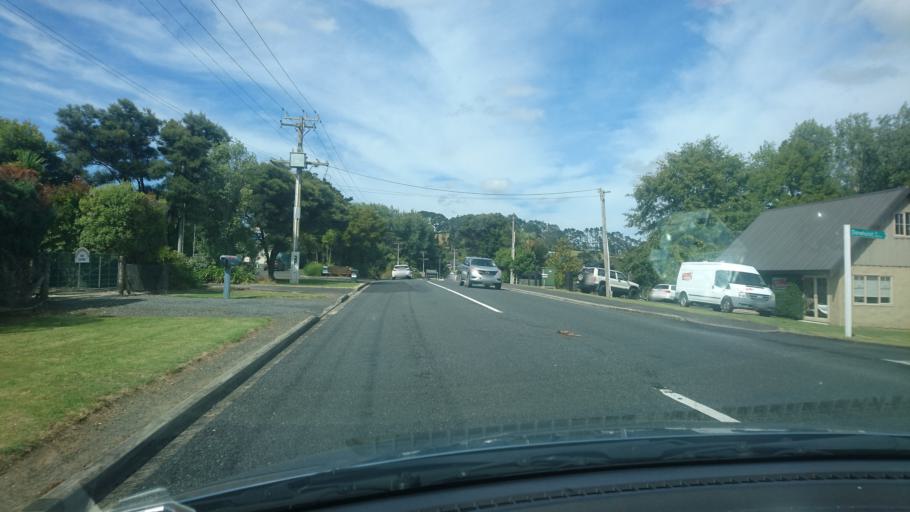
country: NZ
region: Auckland
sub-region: Auckland
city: Muriwai Beach
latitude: -36.7730
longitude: 174.4903
